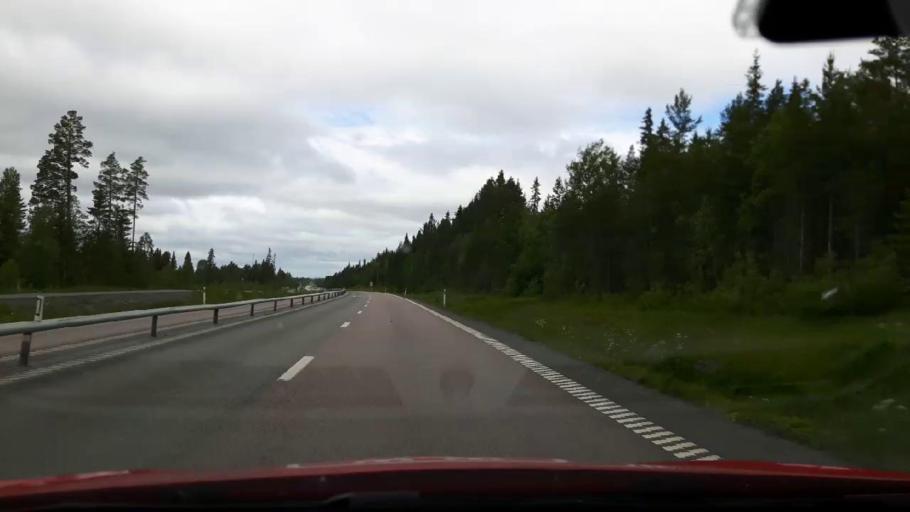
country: SE
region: Jaemtland
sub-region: Krokoms Kommun
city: Krokom
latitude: 63.2752
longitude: 14.5318
